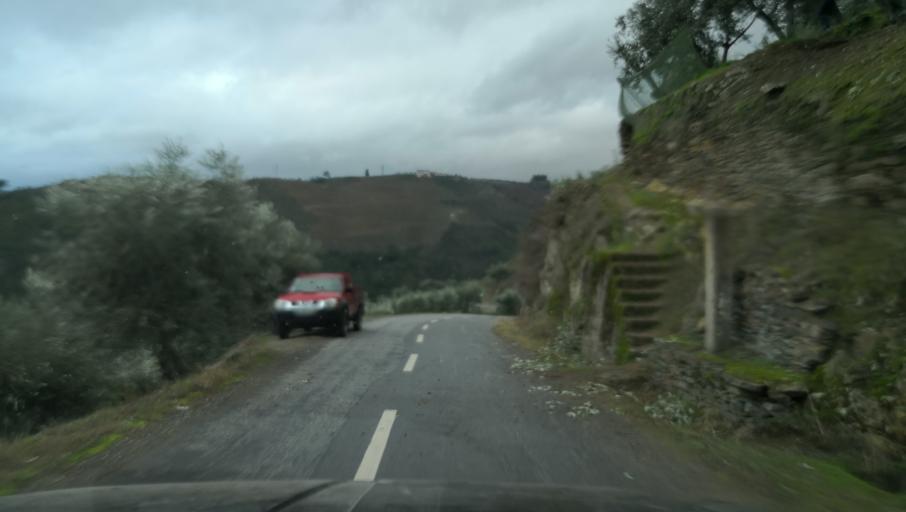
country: PT
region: Vila Real
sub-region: Santa Marta de Penaguiao
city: Santa Marta de Penaguiao
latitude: 41.2182
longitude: -7.7532
